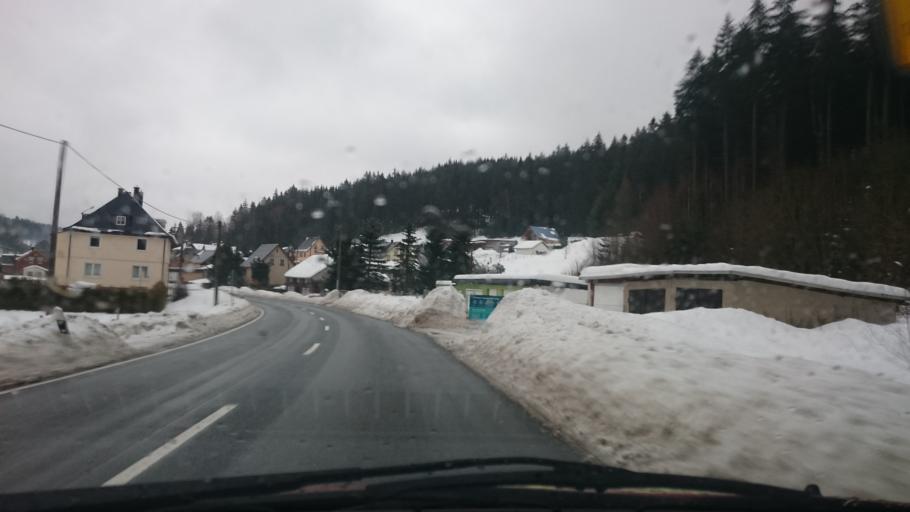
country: DE
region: Saxony
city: Zwota
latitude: 50.3472
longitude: 12.4129
